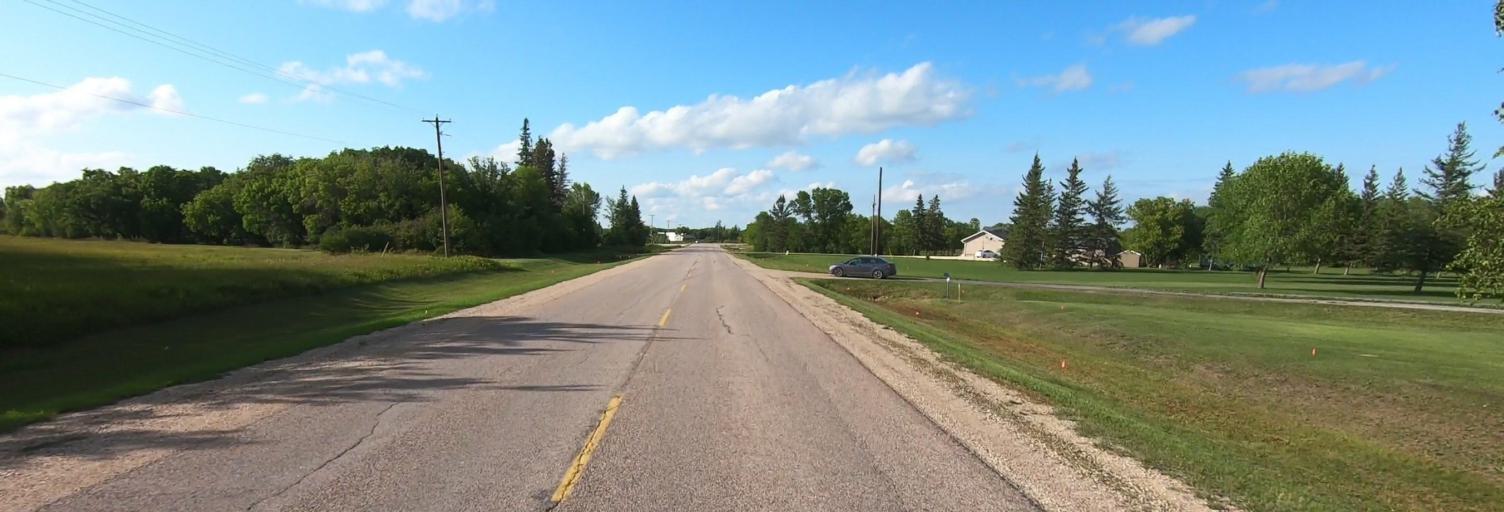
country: CA
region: Manitoba
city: Selkirk
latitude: 50.2083
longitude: -96.8404
